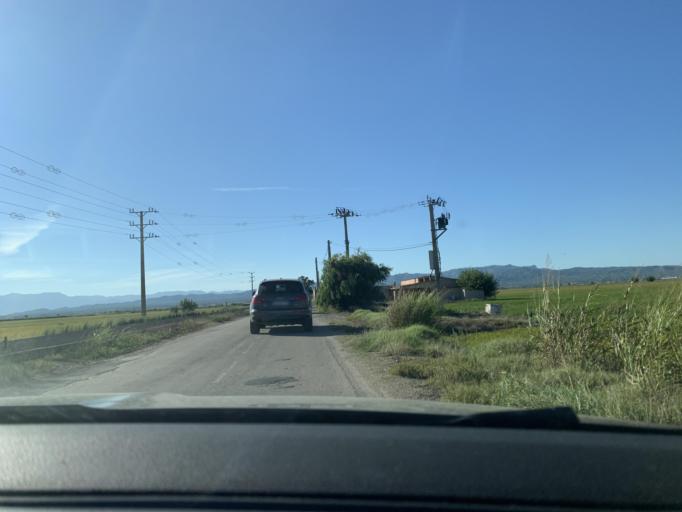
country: ES
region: Catalonia
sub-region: Provincia de Tarragona
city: Deltebre
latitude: 40.7500
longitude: 0.7248
